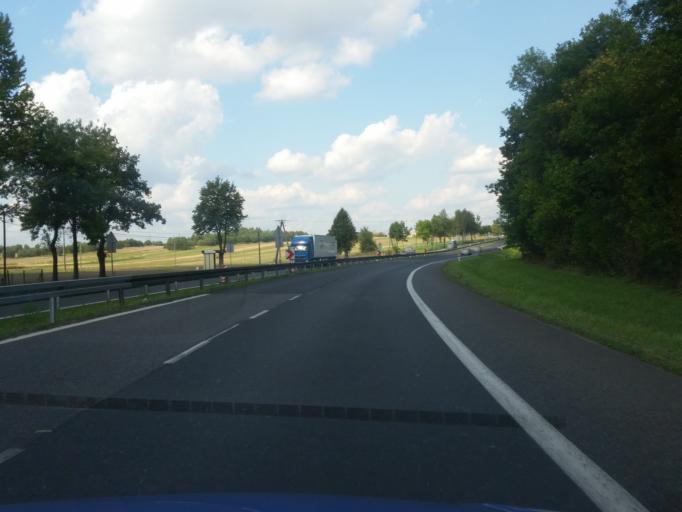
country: PL
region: Silesian Voivodeship
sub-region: Powiat myszkowski
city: Kozieglowy
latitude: 50.5414
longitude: 19.1810
